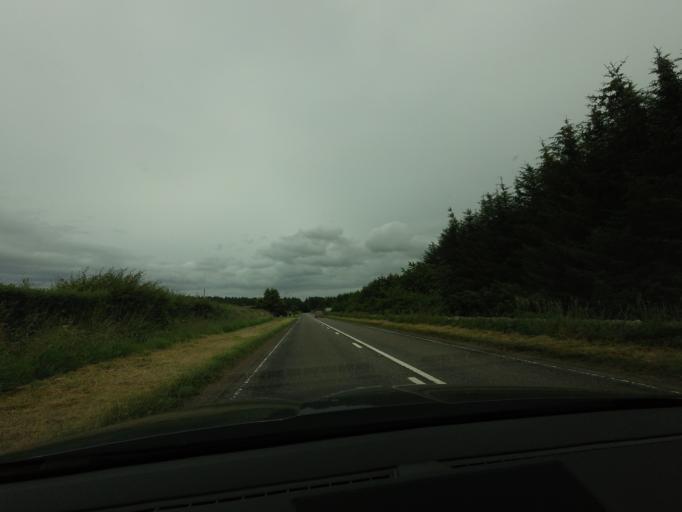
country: GB
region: Scotland
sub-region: Moray
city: Findochty
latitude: 57.6755
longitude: -2.9062
